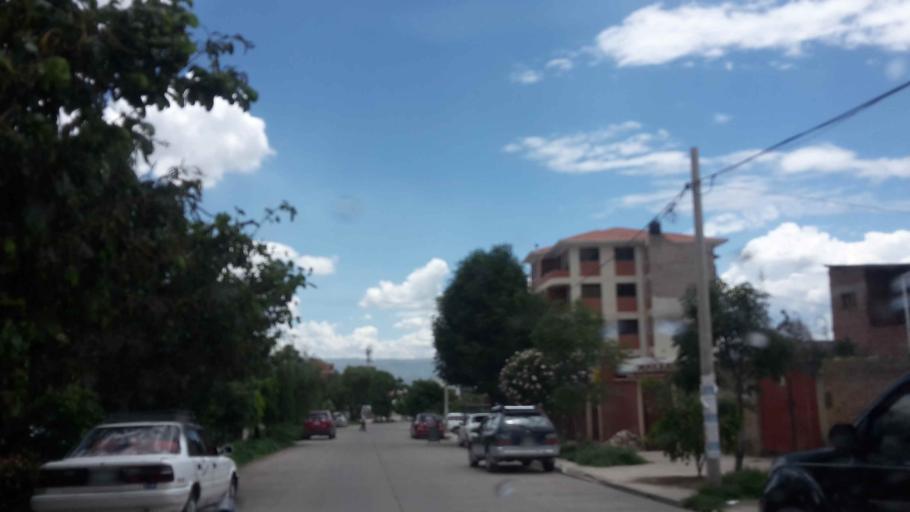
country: BO
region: Cochabamba
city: Cochabamba
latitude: -17.3529
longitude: -66.1828
